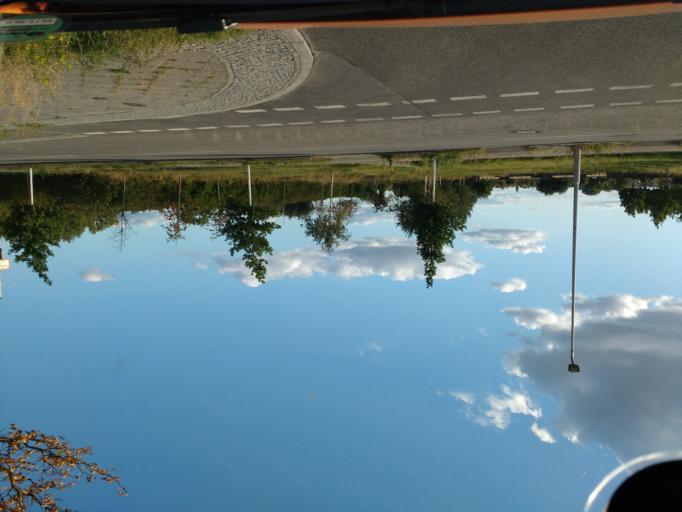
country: DE
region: Berlin
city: Johannisthal
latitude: 52.4331
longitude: 13.5192
